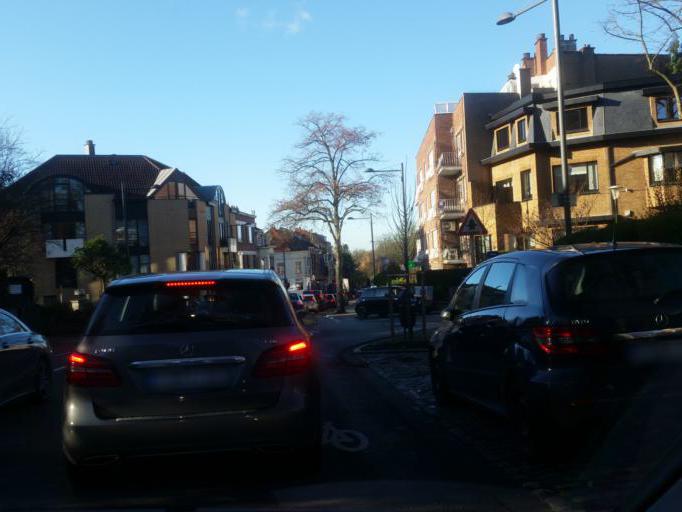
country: BE
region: Flanders
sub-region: Provincie Vlaams-Brabant
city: Linkebeek
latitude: 50.8038
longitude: 4.3604
